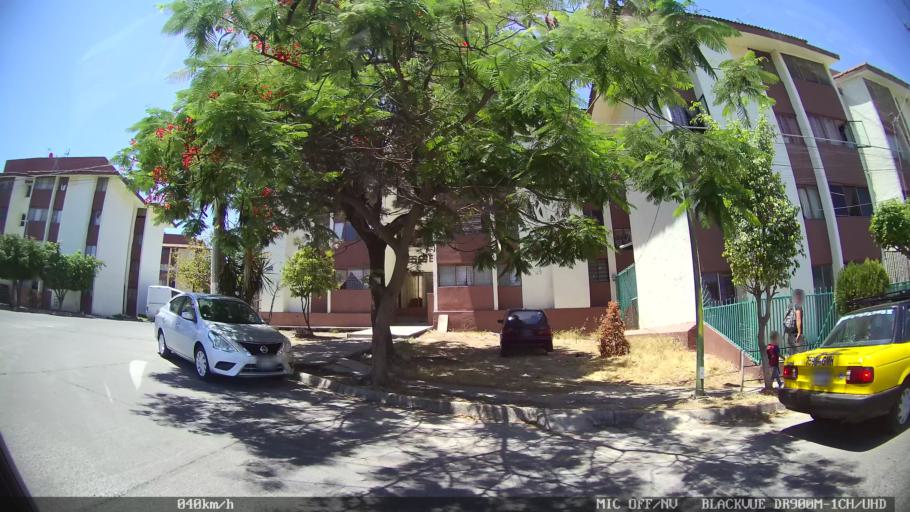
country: MX
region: Jalisco
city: Tlaquepaque
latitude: 20.6856
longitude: -103.2837
